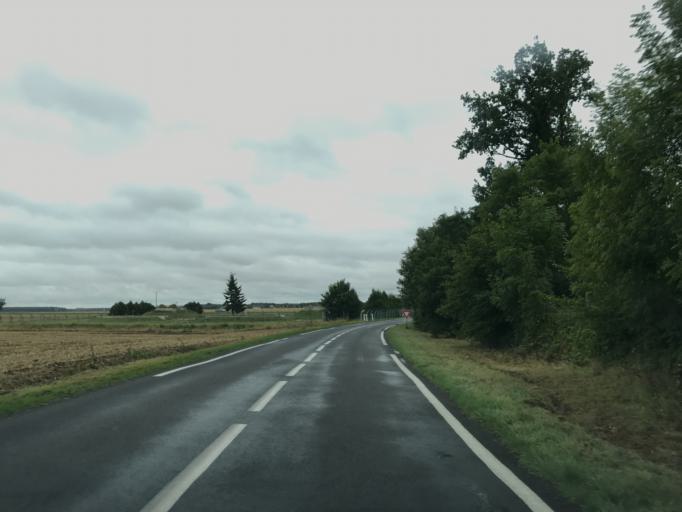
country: FR
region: Haute-Normandie
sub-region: Departement de l'Eure
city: Gravigny
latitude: 49.0161
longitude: 1.2450
